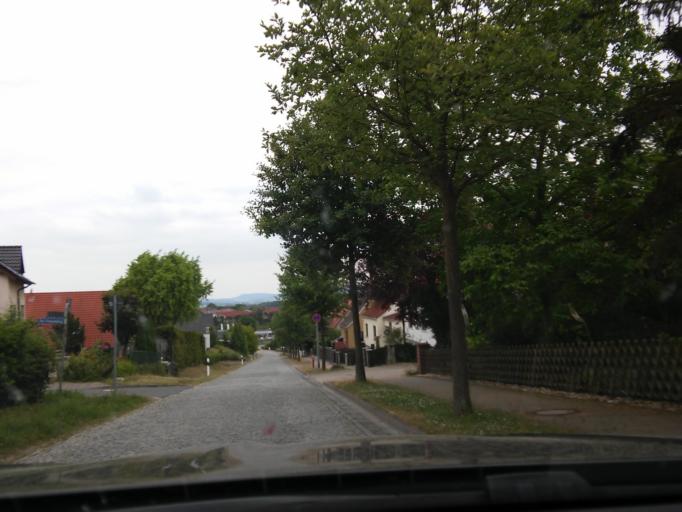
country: DE
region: Thuringia
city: Sondershausen
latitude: 51.3727
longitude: 10.8428
